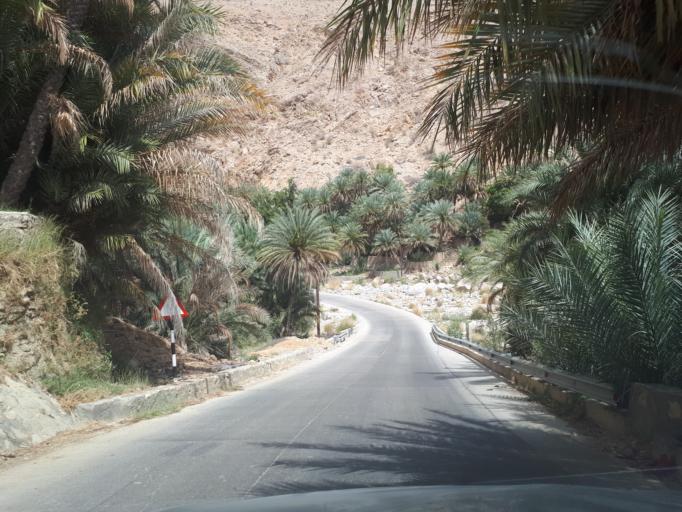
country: OM
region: Ash Sharqiyah
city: Badiyah
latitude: 22.6054
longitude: 59.0872
